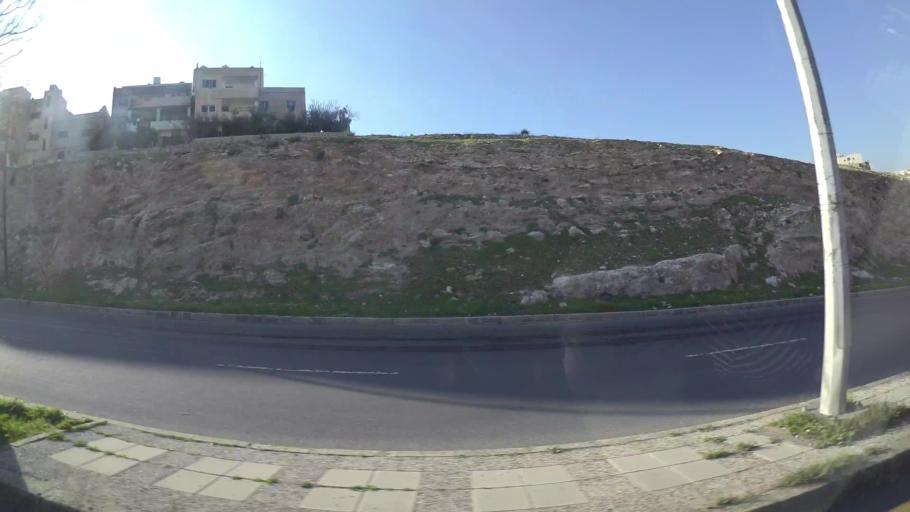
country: JO
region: Amman
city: Amman
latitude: 31.9748
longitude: 35.9691
